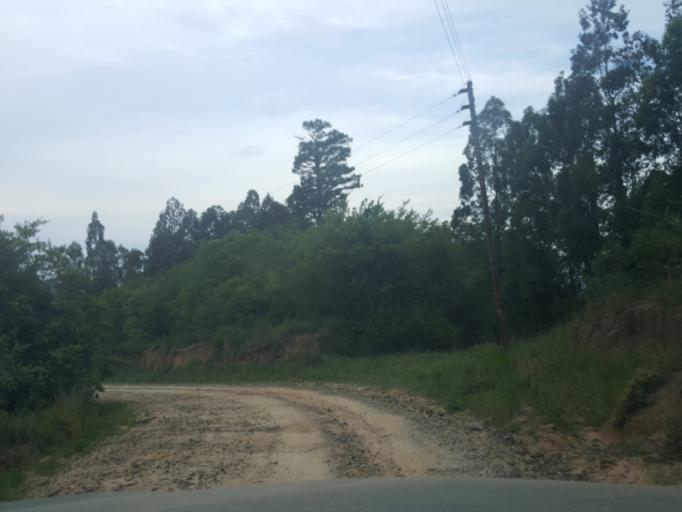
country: ZA
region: Limpopo
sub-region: Mopani District Municipality
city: Hoedspruit
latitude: -24.5962
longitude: 30.8749
